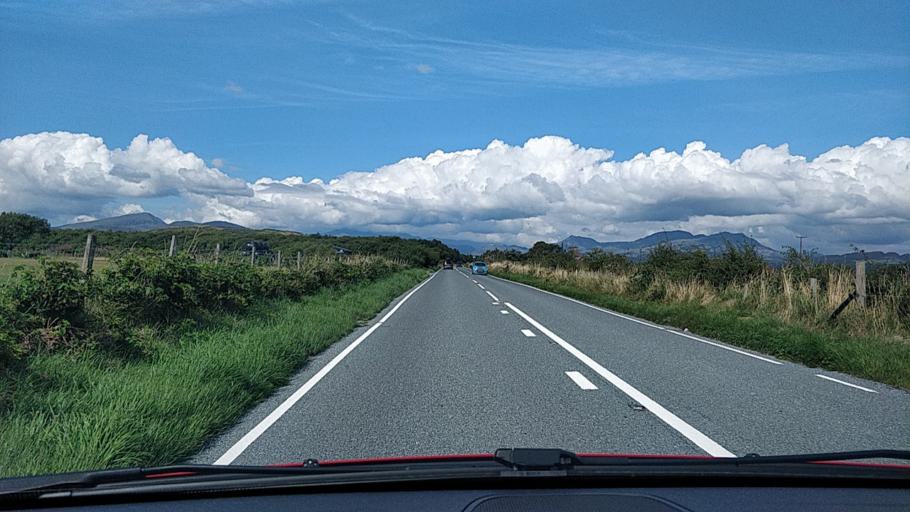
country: GB
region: Wales
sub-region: Gwynedd
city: Llanfair
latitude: 52.8751
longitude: -4.1049
